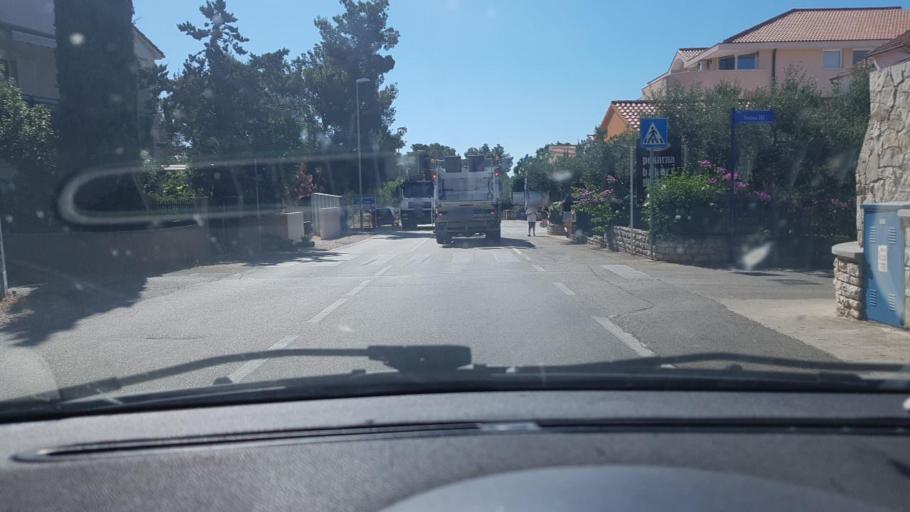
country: HR
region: Sibensko-Kniniska
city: Vodice
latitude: 43.7501
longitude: 15.7971
